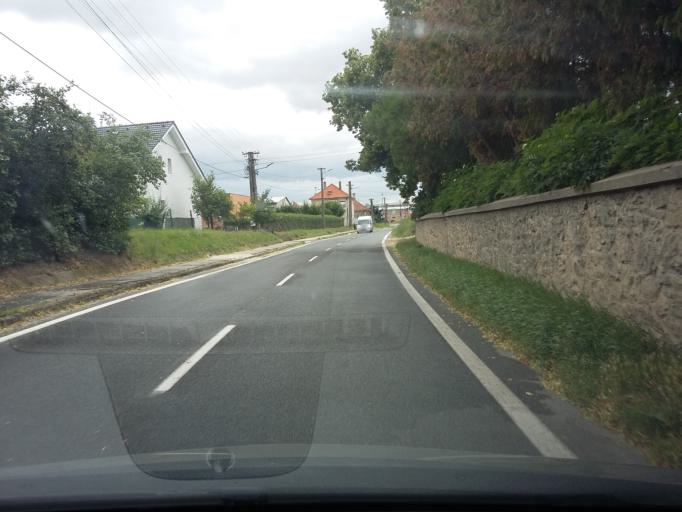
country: SK
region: Trnavsky
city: Vrbove
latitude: 48.6185
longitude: 17.7213
